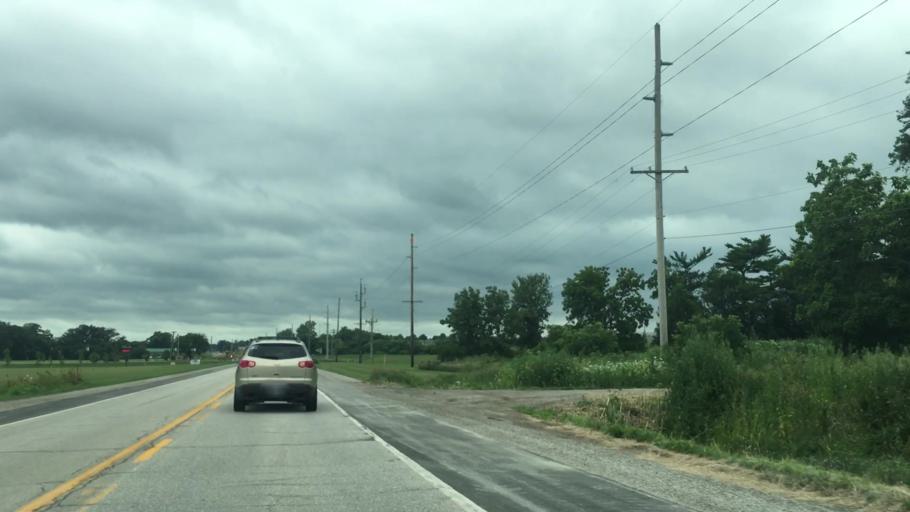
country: US
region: Iowa
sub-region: Johnson County
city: Tiffin
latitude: 41.7056
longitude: -91.6435
